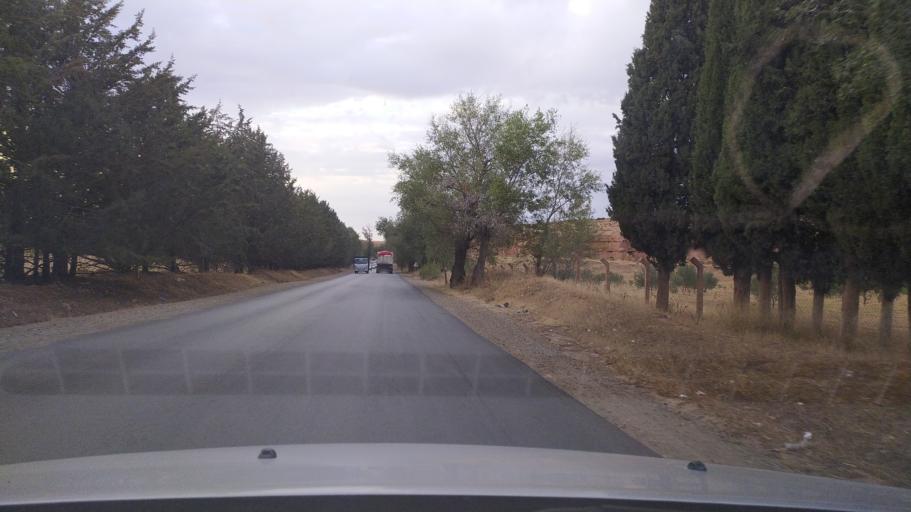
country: DZ
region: Tiaret
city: Frenda
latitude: 35.0466
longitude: 1.0829
